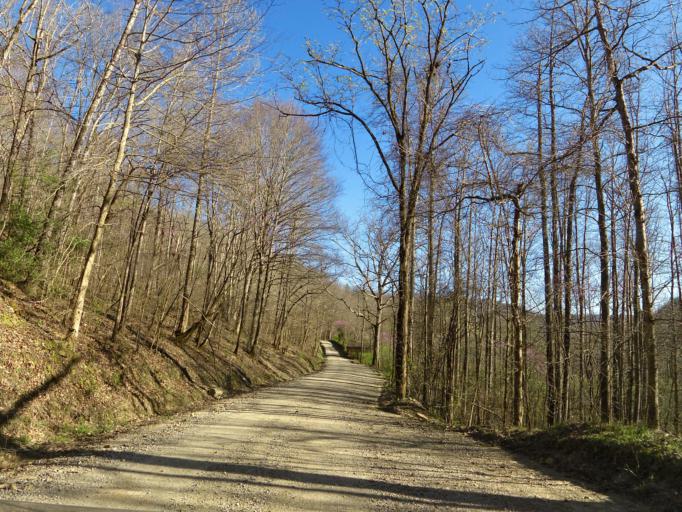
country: US
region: Tennessee
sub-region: Roane County
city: Oliver Springs
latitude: 36.2270
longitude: -84.4159
